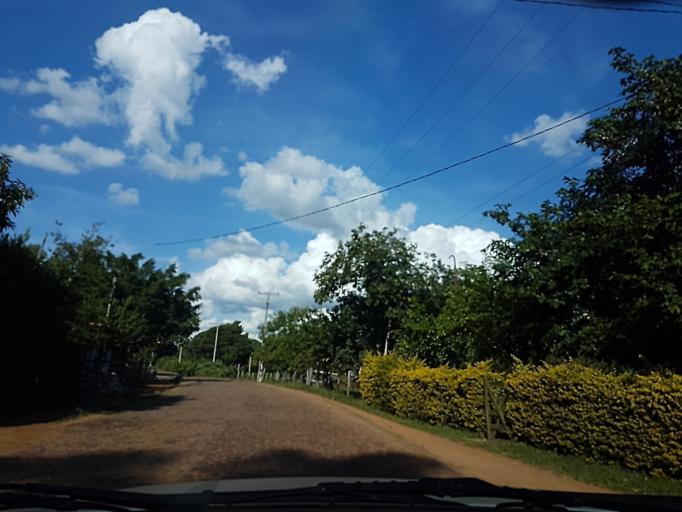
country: PY
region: Cordillera
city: Arroyos y Esteros
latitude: -24.9975
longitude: -57.1691
